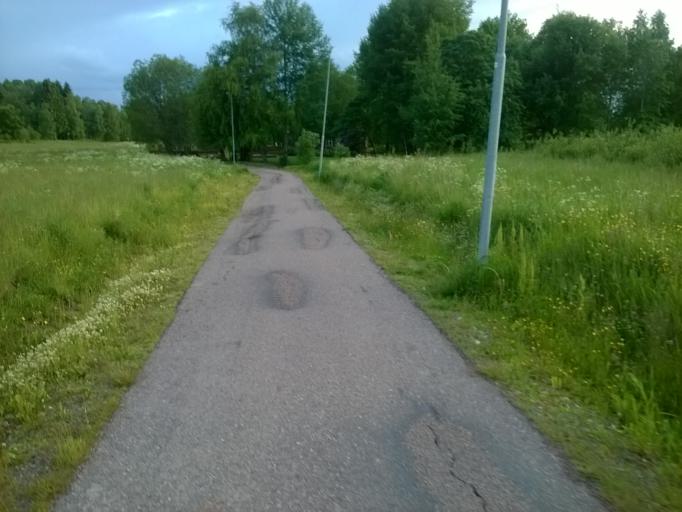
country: SE
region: Dalarna
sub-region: Saters Kommun
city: Saeter
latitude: 60.3441
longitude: 15.7473
